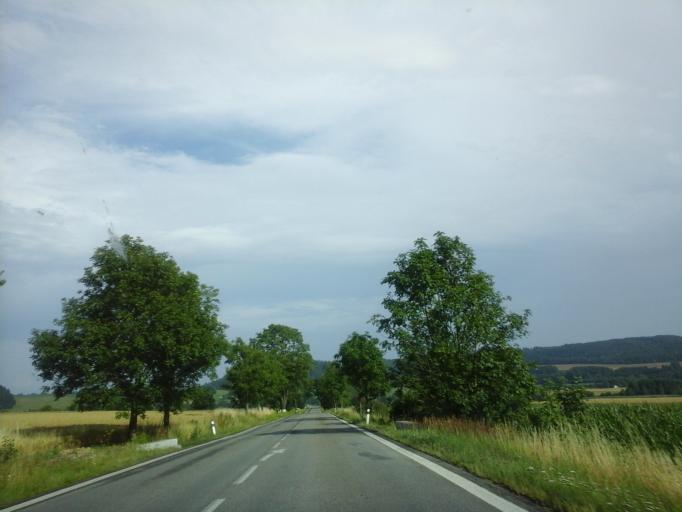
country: CZ
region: Olomoucky
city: Stity
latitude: 49.9954
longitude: 16.7735
